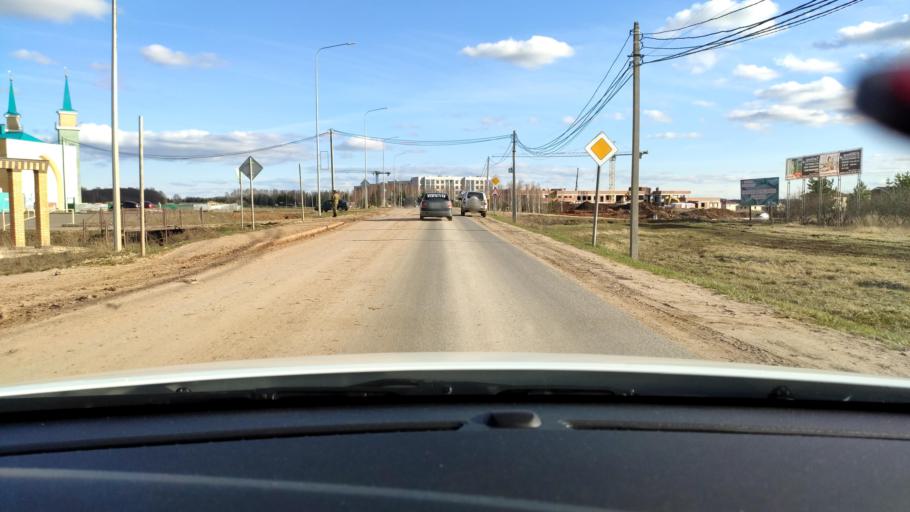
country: RU
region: Tatarstan
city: Vysokaya Gora
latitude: 55.9032
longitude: 49.3239
